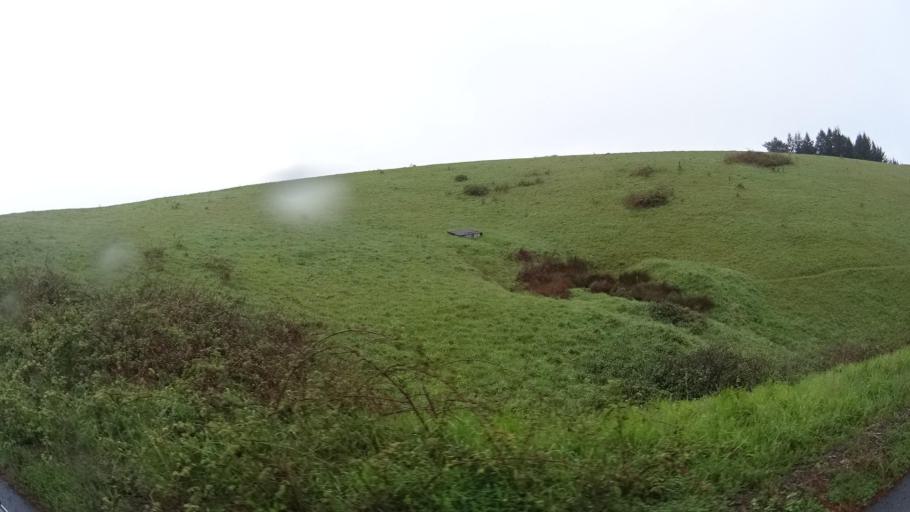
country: US
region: California
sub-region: Humboldt County
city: Westhaven-Moonstone
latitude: 41.1669
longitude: -123.9161
